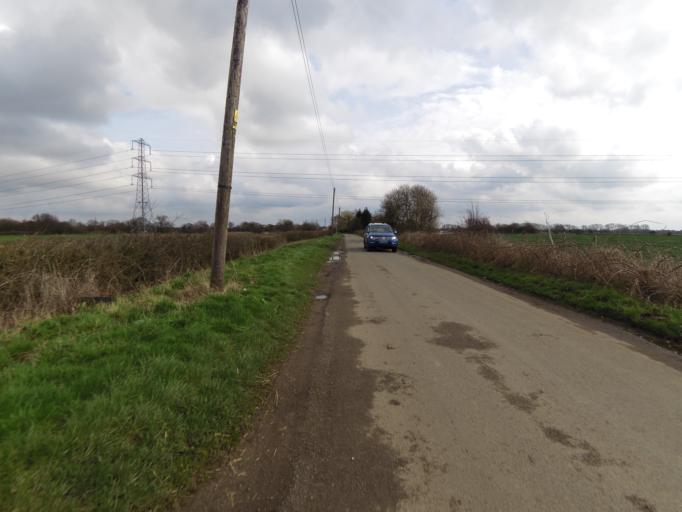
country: GB
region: England
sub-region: Doncaster
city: Moss
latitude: 53.6066
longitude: -1.0895
